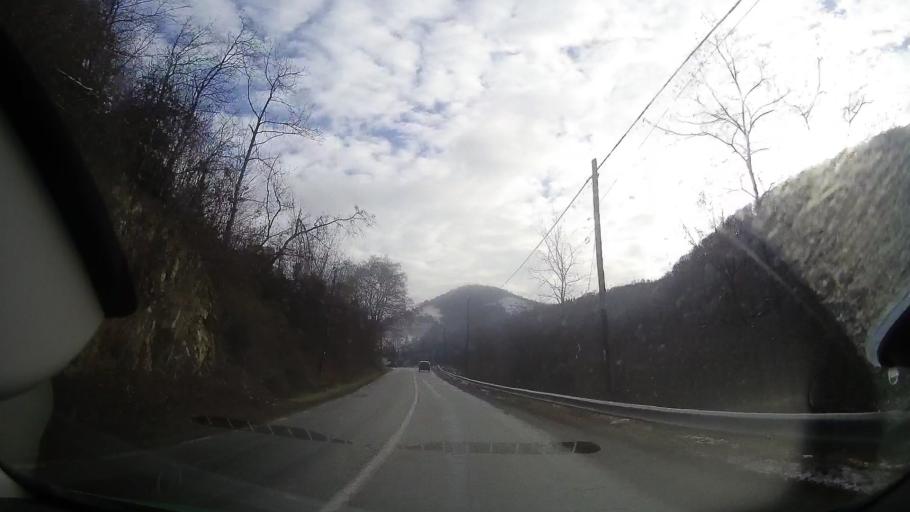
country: RO
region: Alba
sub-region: Oras Baia de Aries
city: Baia de Aries
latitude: 46.3750
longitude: 23.2518
